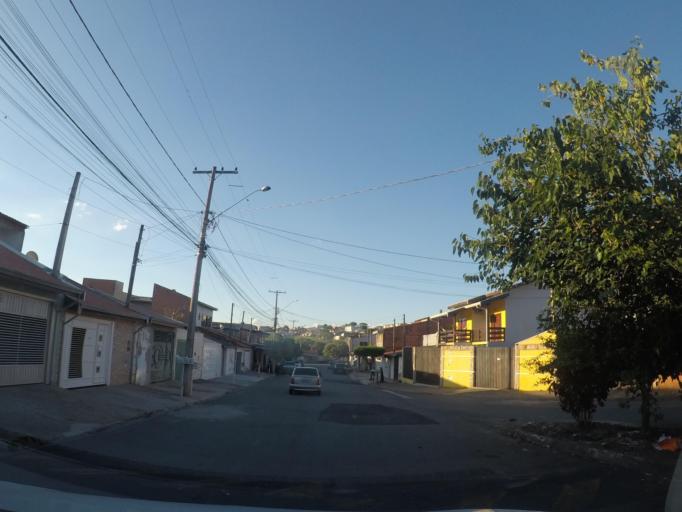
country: BR
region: Sao Paulo
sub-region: Sumare
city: Sumare
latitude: -22.8252
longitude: -47.2486
